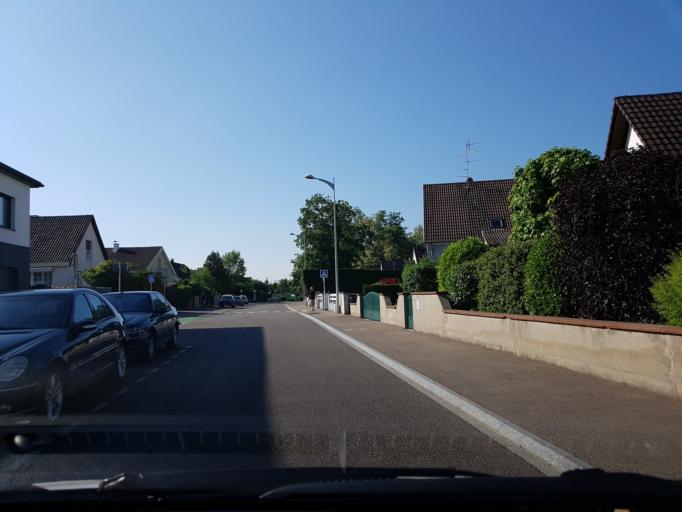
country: FR
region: Alsace
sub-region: Departement du Haut-Rhin
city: Rixheim
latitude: 47.7525
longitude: 7.3895
